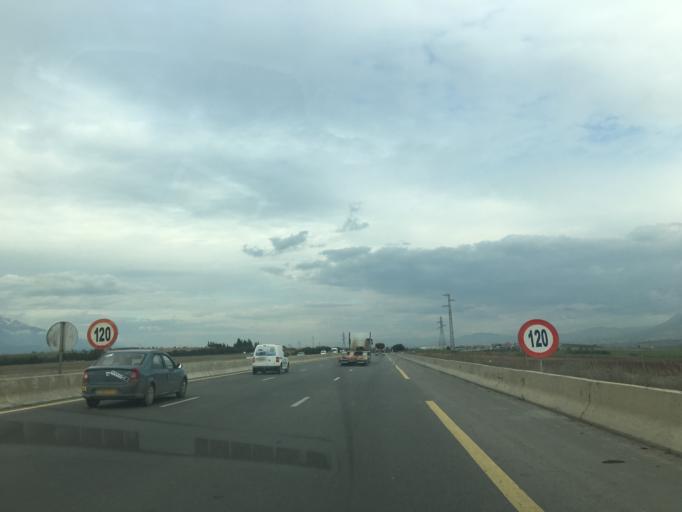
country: DZ
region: Bouira
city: Bouira
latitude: 36.3273
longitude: 3.9792
